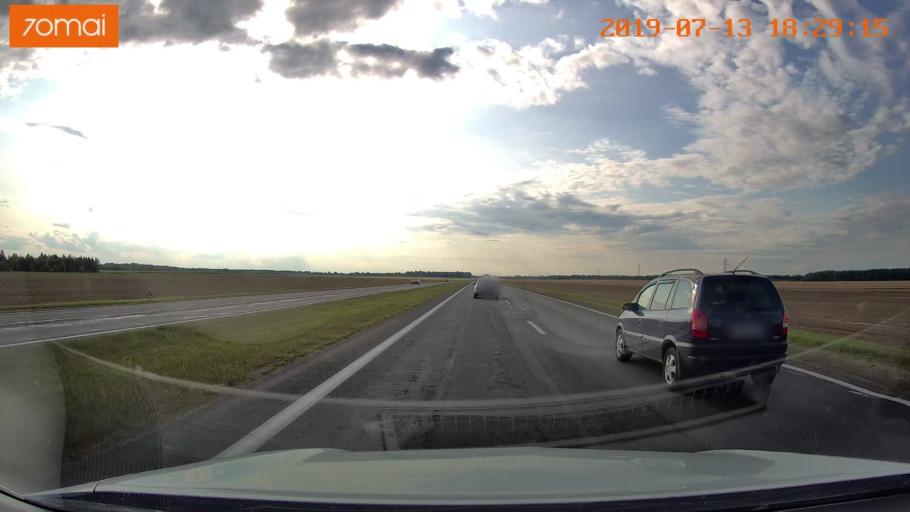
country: BY
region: Minsk
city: Dukora
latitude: 53.6499
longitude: 27.9746
